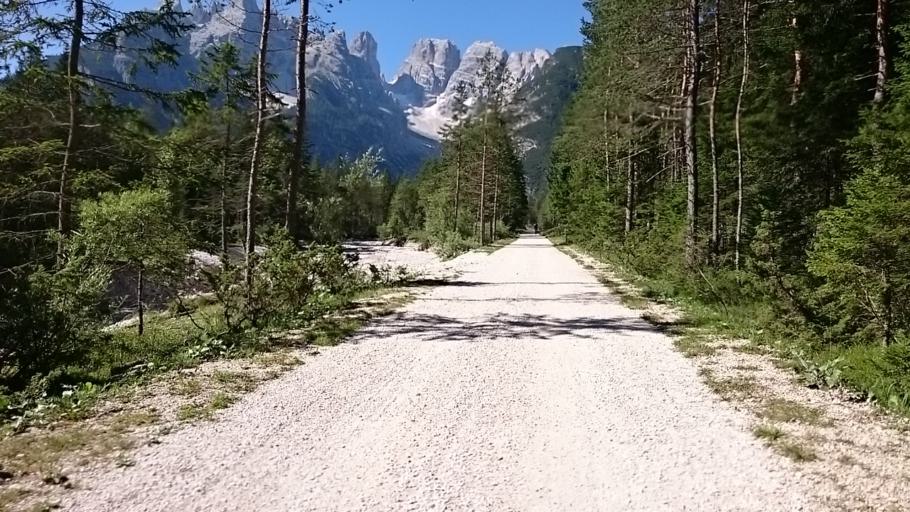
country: IT
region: Trentino-Alto Adige
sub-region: Bolzano
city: Dobbiaco
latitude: 46.6248
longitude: 12.2258
